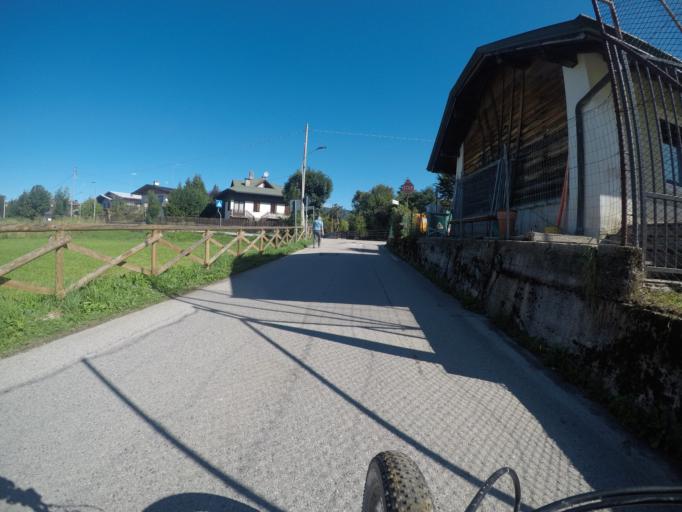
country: IT
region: Veneto
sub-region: Provincia di Vicenza
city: Roana
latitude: 45.8380
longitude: 11.4350
